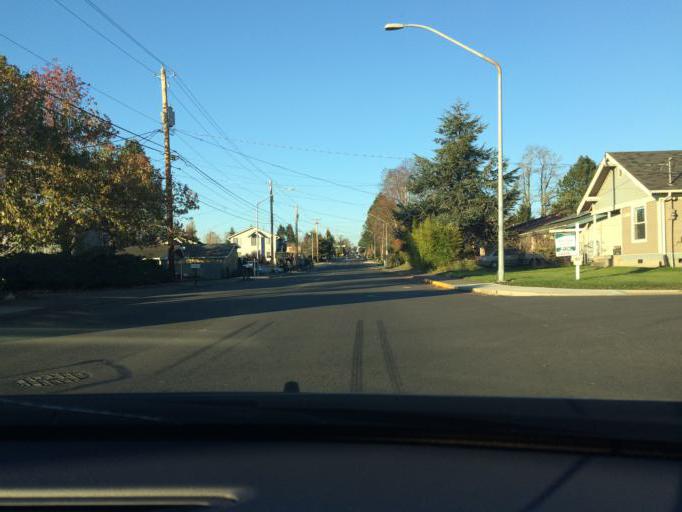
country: US
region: Washington
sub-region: Whatcom County
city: Bellingham
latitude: 48.7602
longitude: -122.4453
